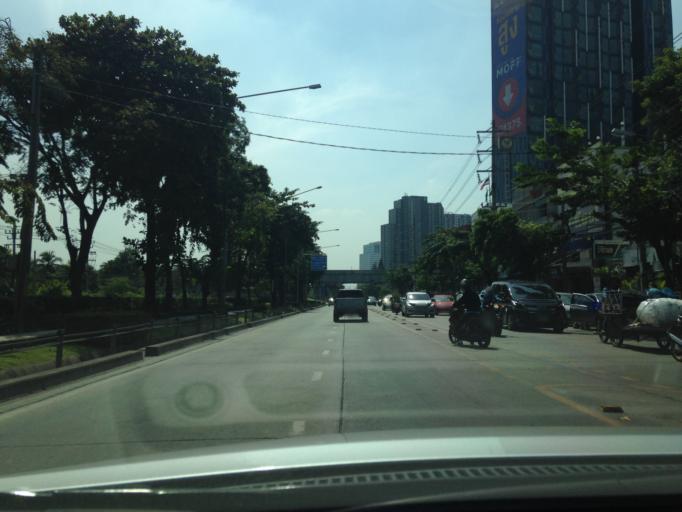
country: TH
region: Bangkok
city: Bang Sue
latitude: 13.8239
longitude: 100.5375
